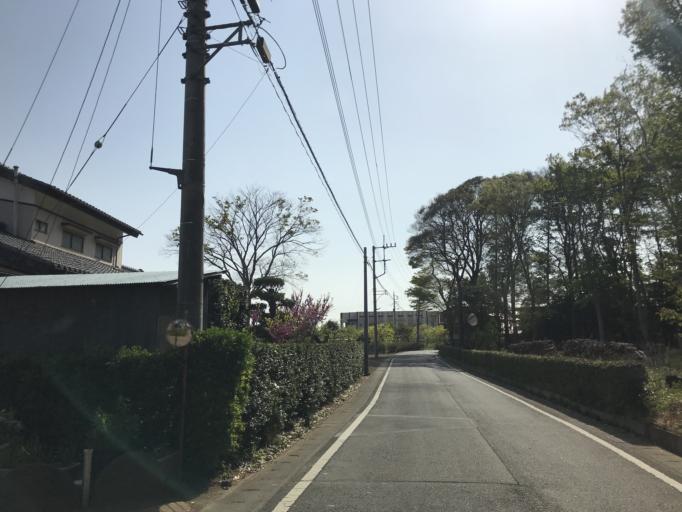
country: JP
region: Ibaraki
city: Mitsukaido
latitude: 35.9731
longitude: 139.9660
